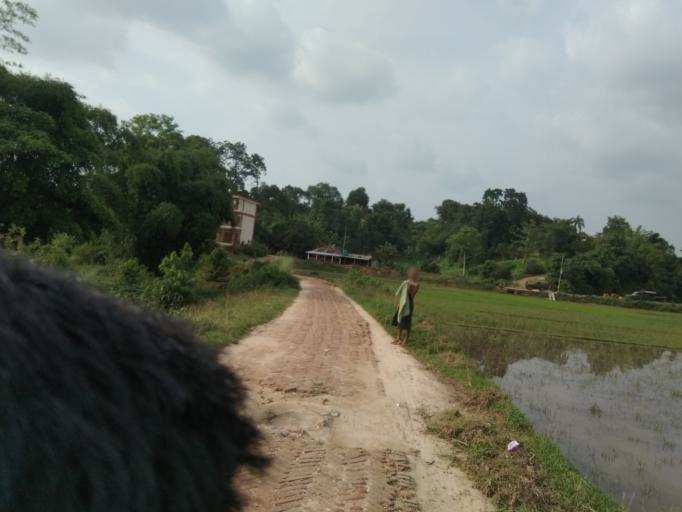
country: BD
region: Chittagong
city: Manikchari
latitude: 22.9342
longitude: 91.9103
